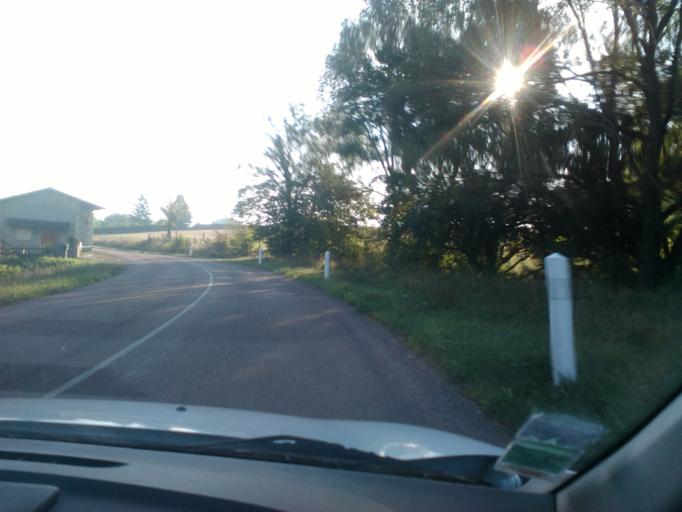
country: FR
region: Lorraine
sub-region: Departement des Vosges
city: Mirecourt
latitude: 48.3039
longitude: 6.1547
